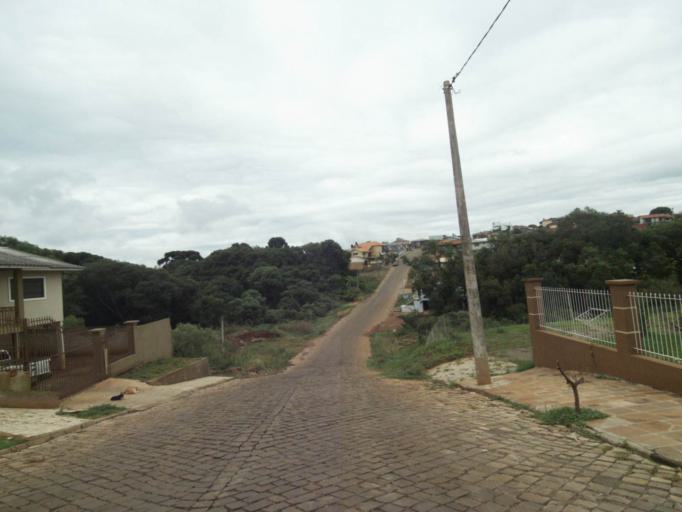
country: BR
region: Rio Grande do Sul
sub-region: Lagoa Vermelha
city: Lagoa Vermelha
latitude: -28.2148
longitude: -51.5279
